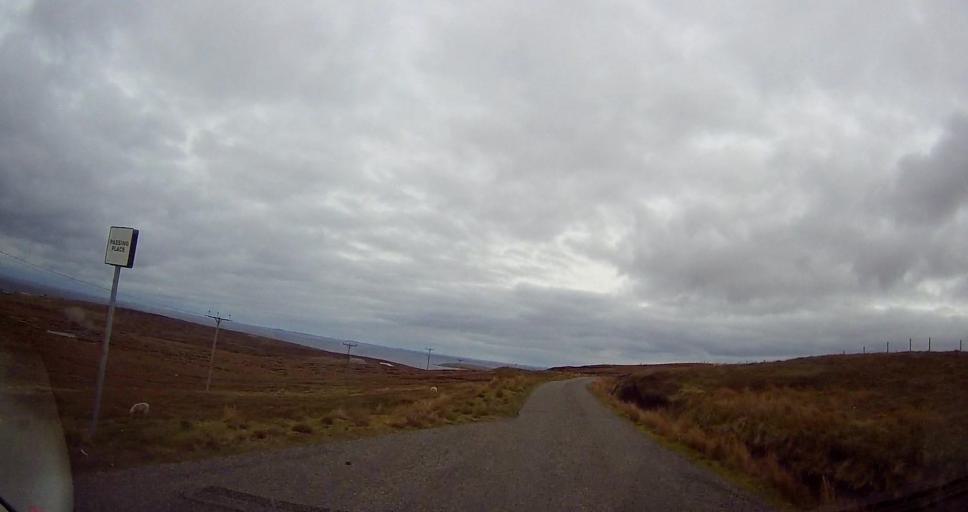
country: GB
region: Scotland
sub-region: Shetland Islands
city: Shetland
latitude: 60.5639
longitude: -1.0643
